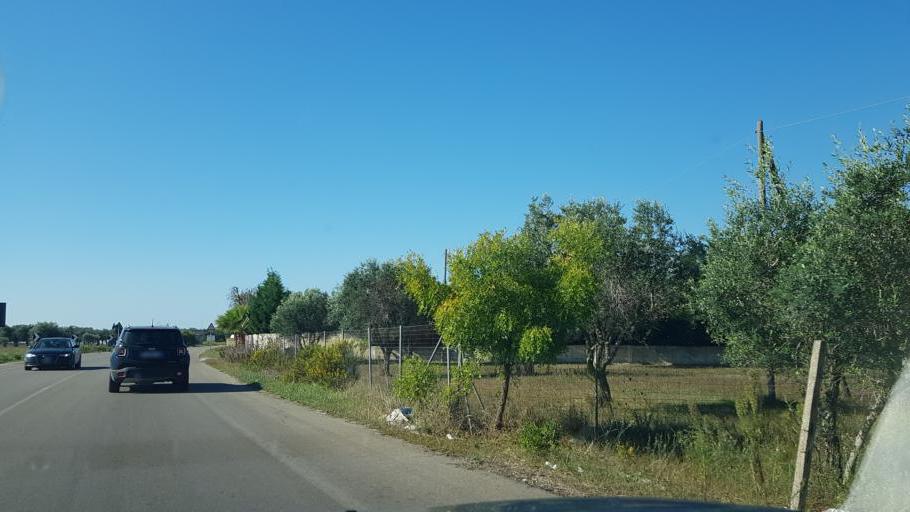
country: IT
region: Apulia
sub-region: Provincia di Lecce
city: Leverano
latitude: 40.3010
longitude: 18.0096
